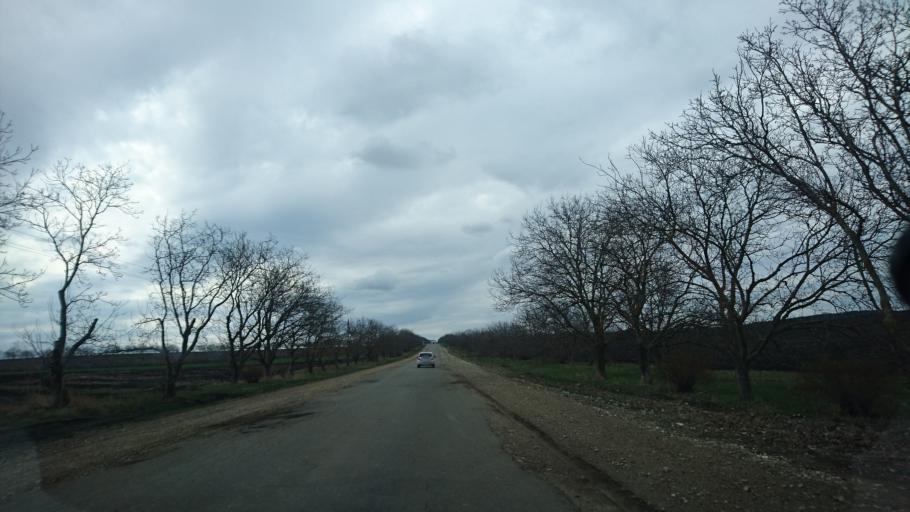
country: MD
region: Gagauzia
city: Comrat
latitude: 46.3127
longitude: 28.5617
